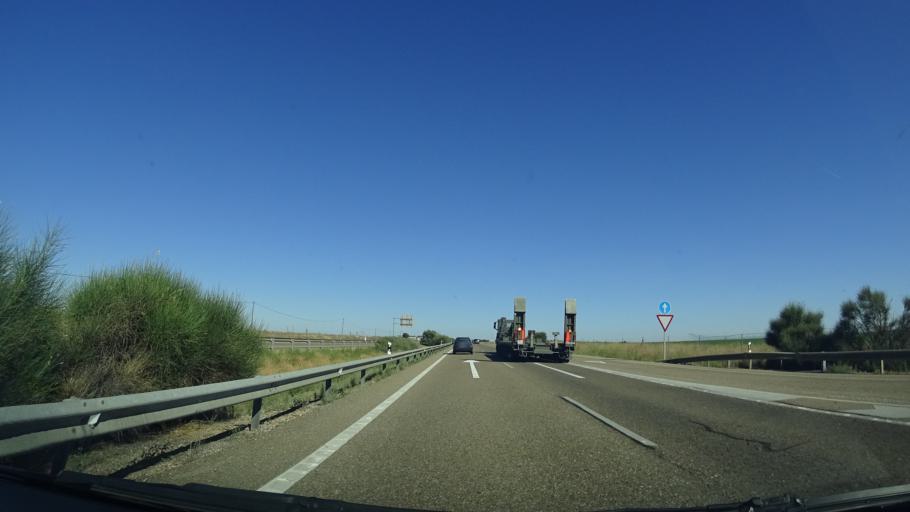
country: ES
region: Castille and Leon
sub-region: Provincia de Valladolid
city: San Pedro de Latarce
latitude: 41.7688
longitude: -5.3039
